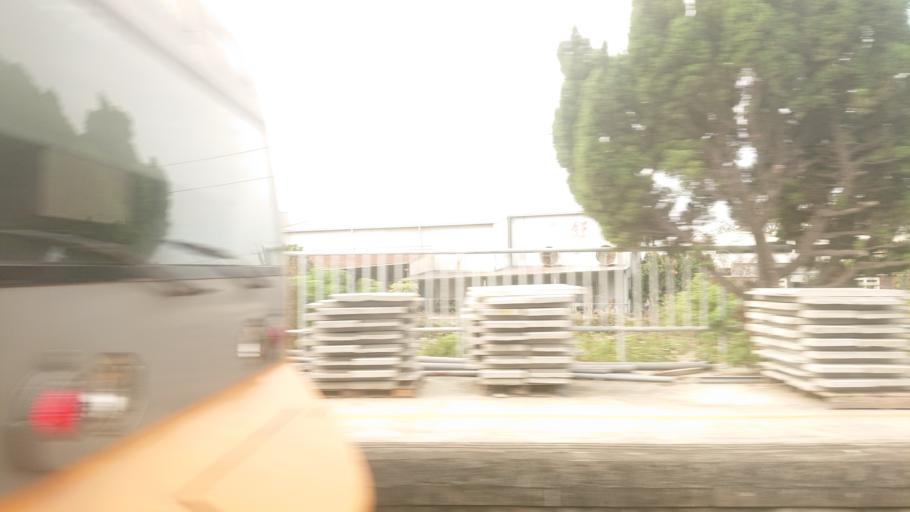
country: TW
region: Taiwan
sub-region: Changhua
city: Chang-hua
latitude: 24.0257
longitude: 120.5368
